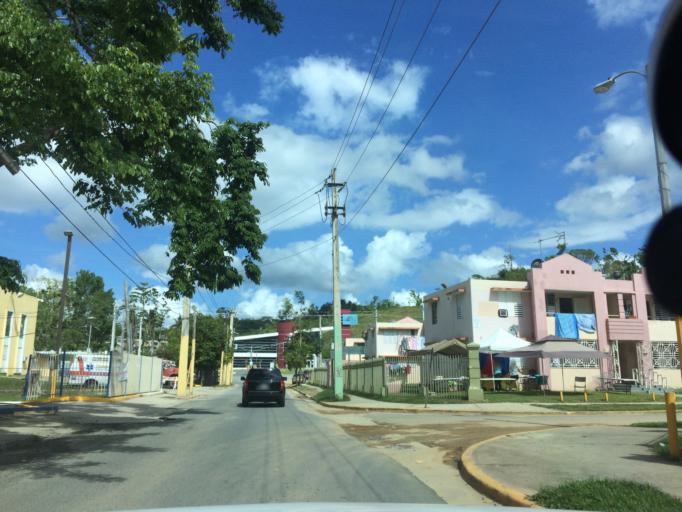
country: PR
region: Utuado
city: Utuado
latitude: 18.2678
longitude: -66.7008
